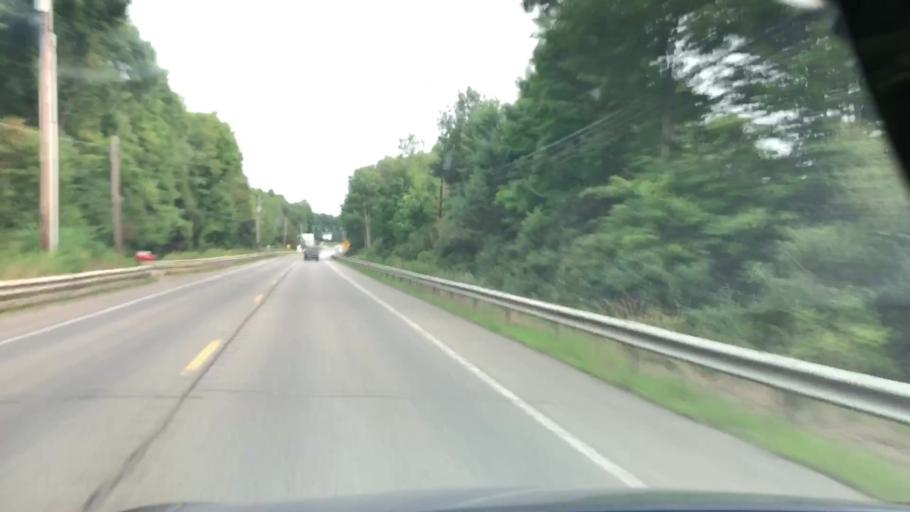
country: US
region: Pennsylvania
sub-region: Crawford County
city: Titusville
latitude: 41.6493
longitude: -79.7191
